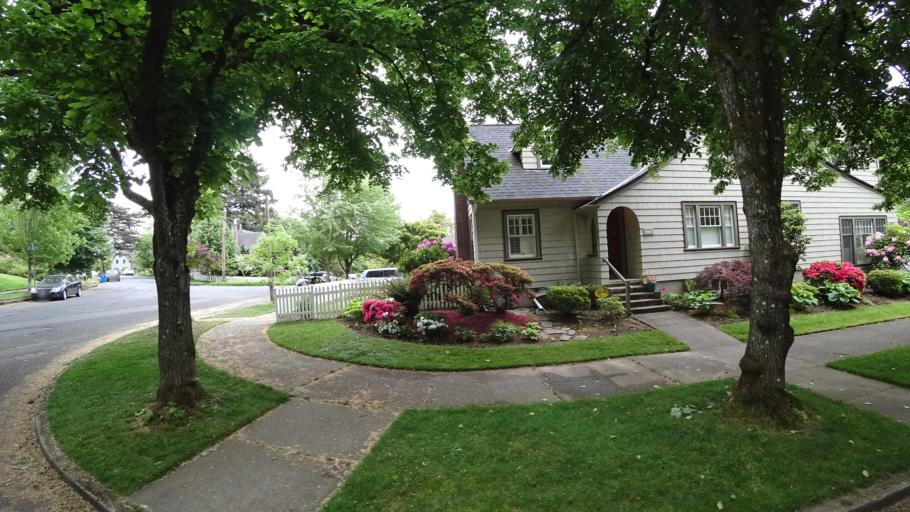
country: US
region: Oregon
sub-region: Multnomah County
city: Portland
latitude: 45.5428
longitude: -122.6191
